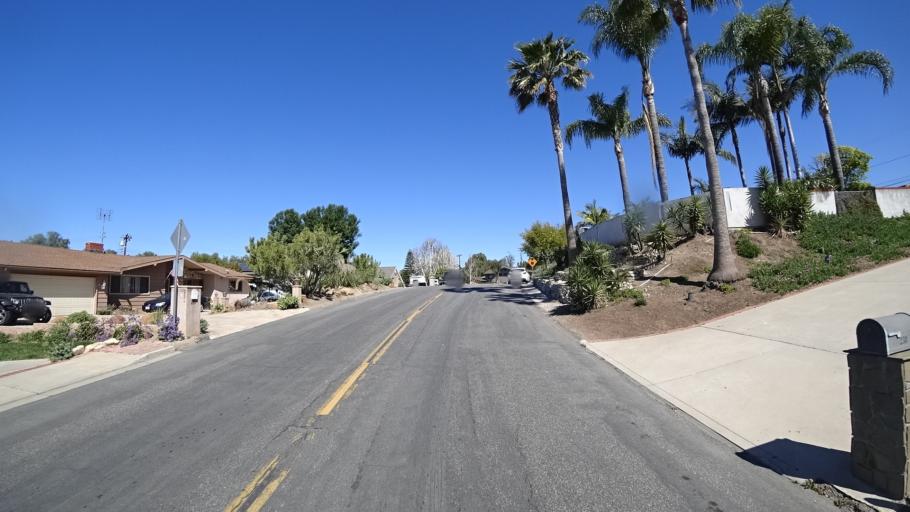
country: US
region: California
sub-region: Ventura County
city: Thousand Oaks
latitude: 34.1816
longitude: -118.8590
